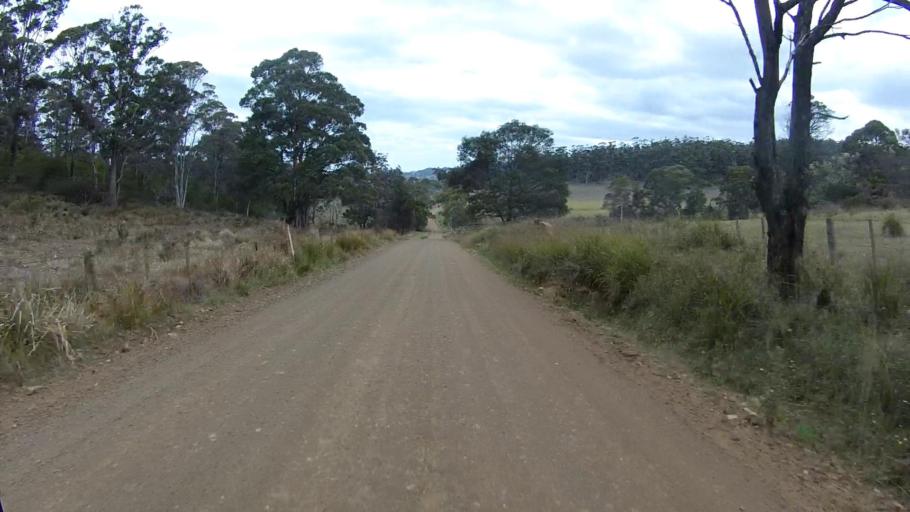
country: AU
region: Tasmania
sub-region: Sorell
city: Sorell
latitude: -42.6122
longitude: 147.9309
